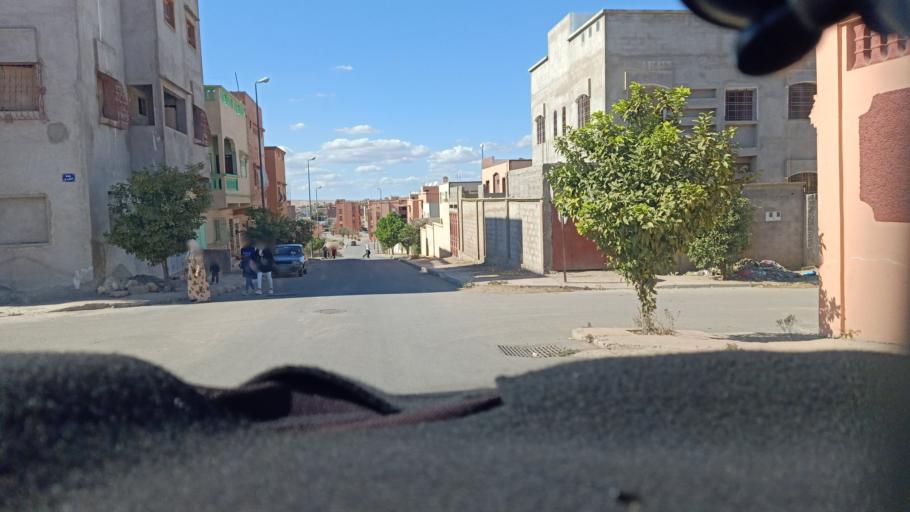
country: MA
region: Doukkala-Abda
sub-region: Safi
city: Youssoufia
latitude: 32.2393
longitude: -8.5326
